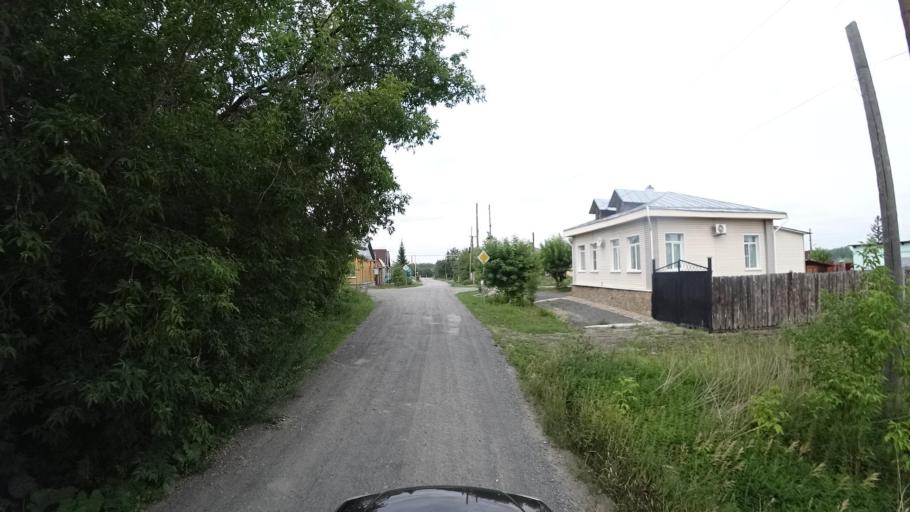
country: RU
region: Sverdlovsk
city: Kamyshlov
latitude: 56.8497
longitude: 62.6969
